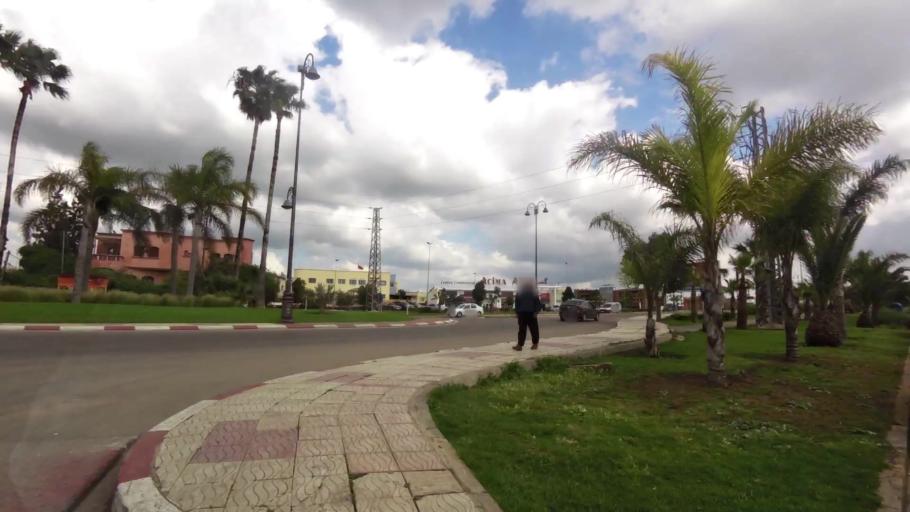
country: MA
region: Chaouia-Ouardigha
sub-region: Settat Province
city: Berrechid
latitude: 33.2804
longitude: -7.5904
